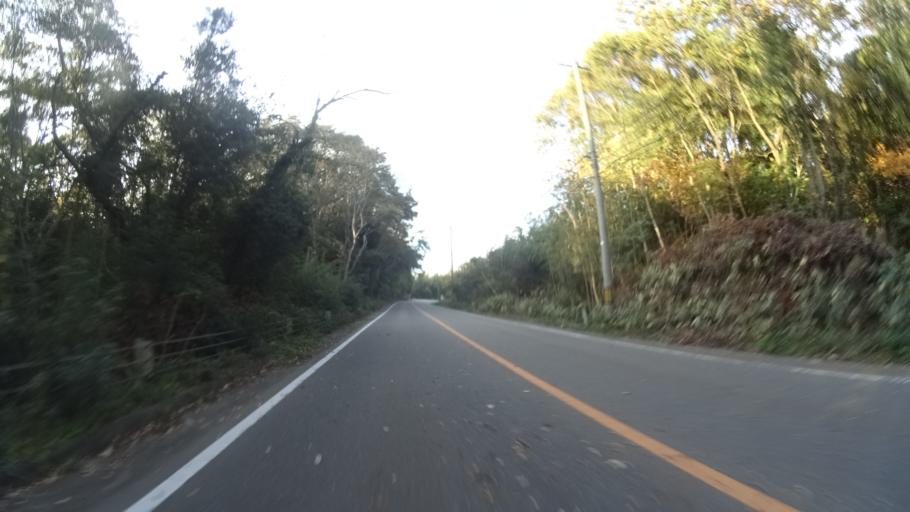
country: JP
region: Ishikawa
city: Nanao
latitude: 37.1688
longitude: 136.7145
